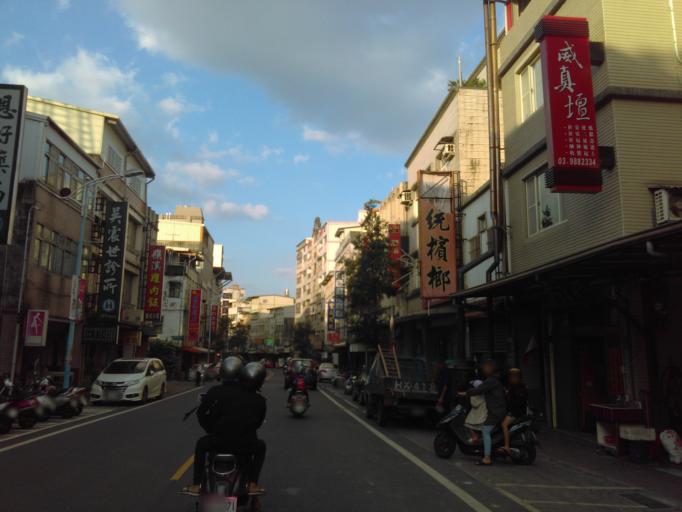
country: TW
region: Taiwan
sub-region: Yilan
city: Yilan
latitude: 24.8190
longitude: 121.7699
